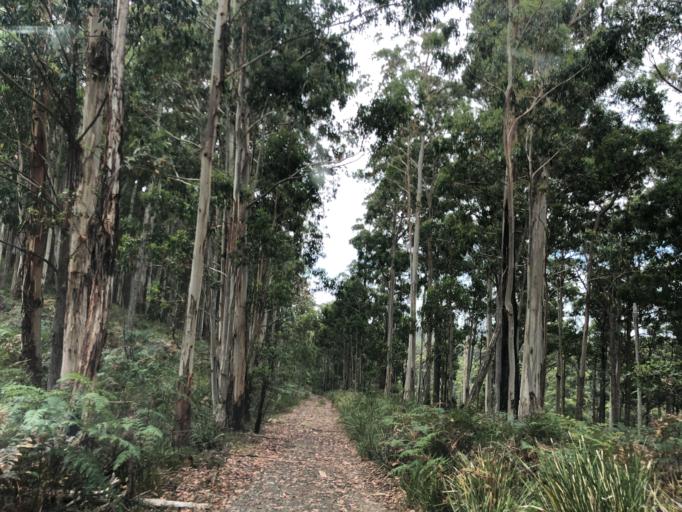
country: AU
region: Victoria
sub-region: Moorabool
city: Bacchus Marsh
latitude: -37.4464
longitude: 144.2457
